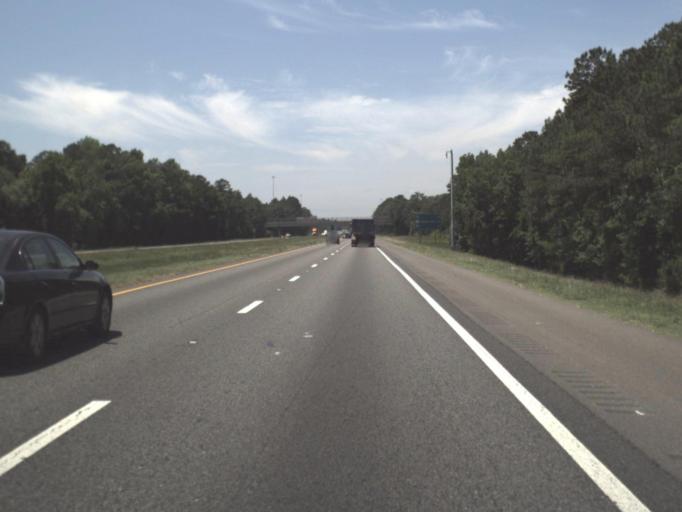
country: US
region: Florida
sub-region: Duval County
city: Jacksonville
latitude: 30.4601
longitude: -81.6642
